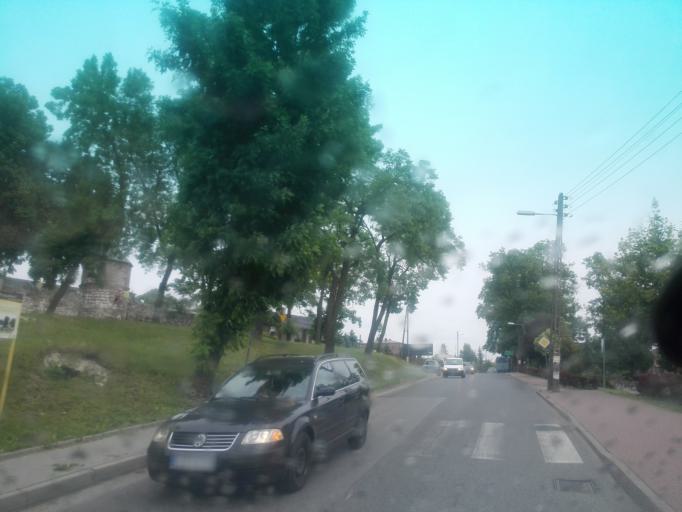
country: PL
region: Silesian Voivodeship
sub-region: Powiat czestochowski
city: Mstow
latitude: 50.8320
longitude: 19.2896
